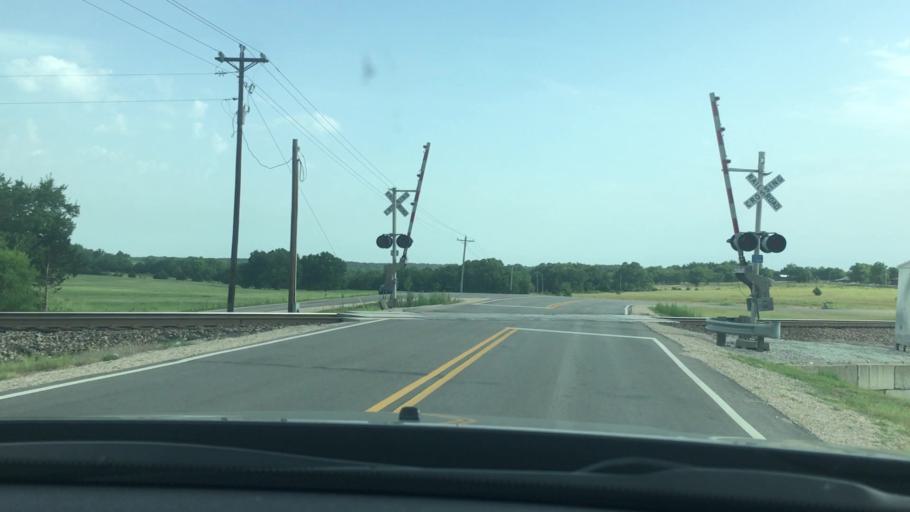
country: US
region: Oklahoma
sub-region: Pontotoc County
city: Byng
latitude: 34.8500
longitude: -96.6170
